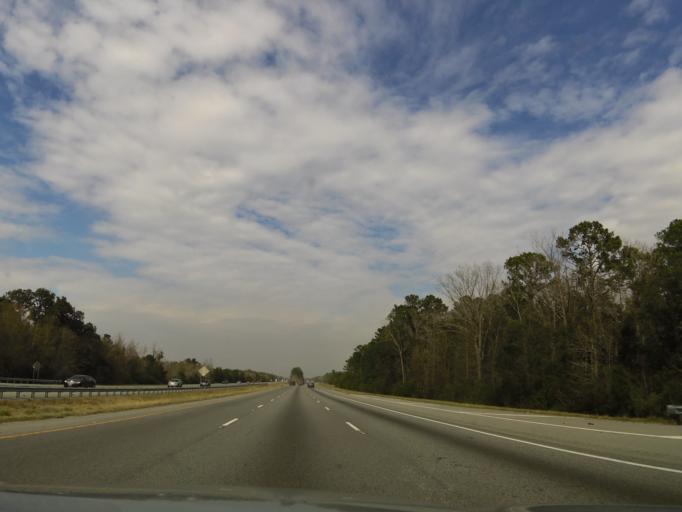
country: US
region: Georgia
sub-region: Liberty County
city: Midway
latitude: 31.7393
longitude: -81.3863
